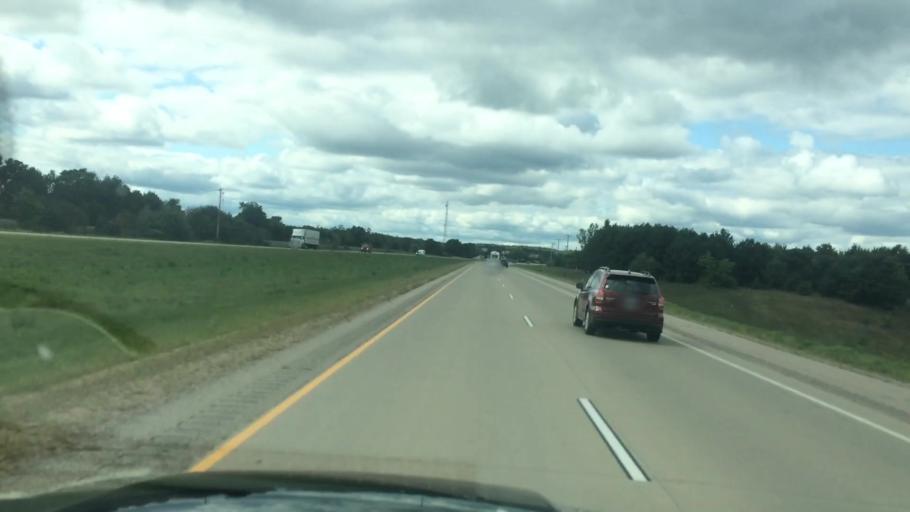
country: US
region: Wisconsin
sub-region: Portage County
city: Plover
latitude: 44.5061
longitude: -89.4136
